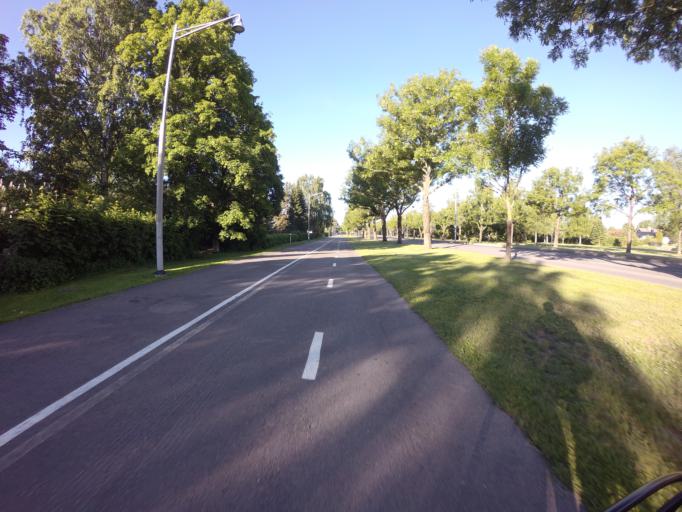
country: FI
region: Varsinais-Suomi
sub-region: Turku
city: Turku
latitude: 60.4683
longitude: 22.2783
